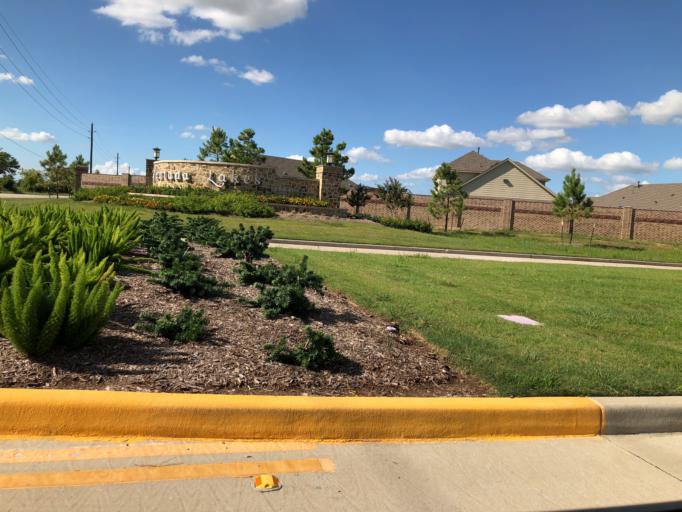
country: US
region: Texas
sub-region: Harris County
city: Katy
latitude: 29.8389
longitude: -95.7901
